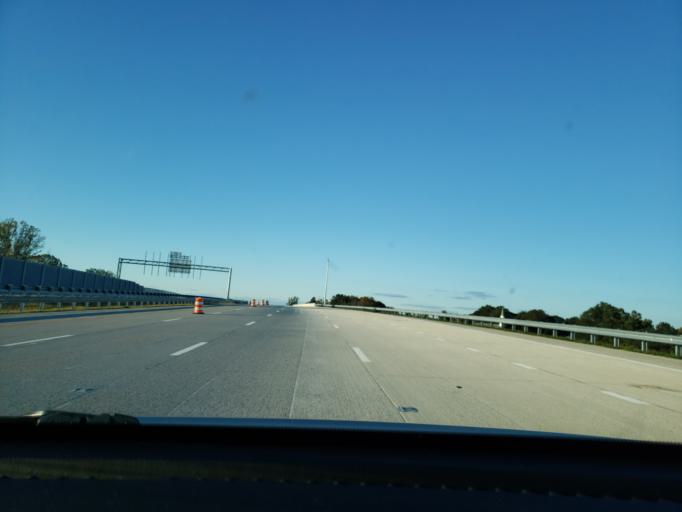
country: US
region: North Carolina
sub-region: Forsyth County
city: Walkertown
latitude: 36.1269
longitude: -80.1294
